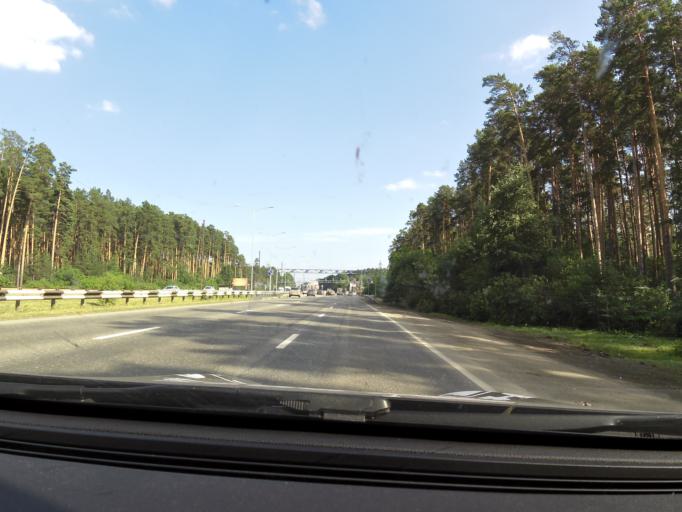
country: RU
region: Sverdlovsk
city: Shirokaya Rechka
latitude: 56.8146
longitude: 60.5140
